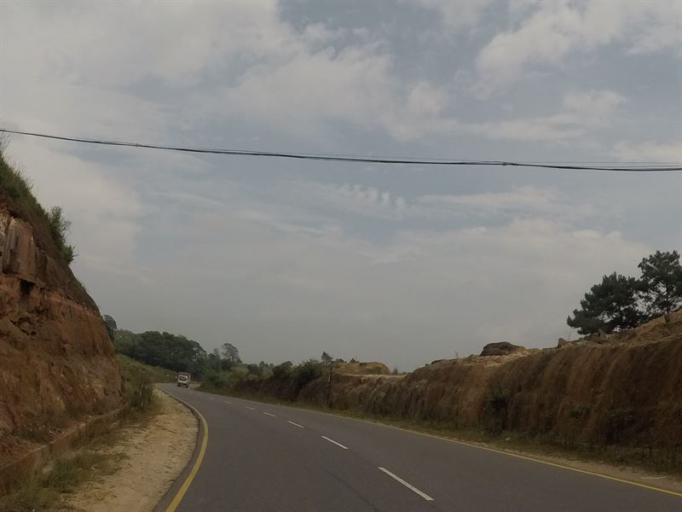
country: IN
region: Meghalaya
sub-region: East Khasi Hills
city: Shillong
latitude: 25.4906
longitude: 92.1815
